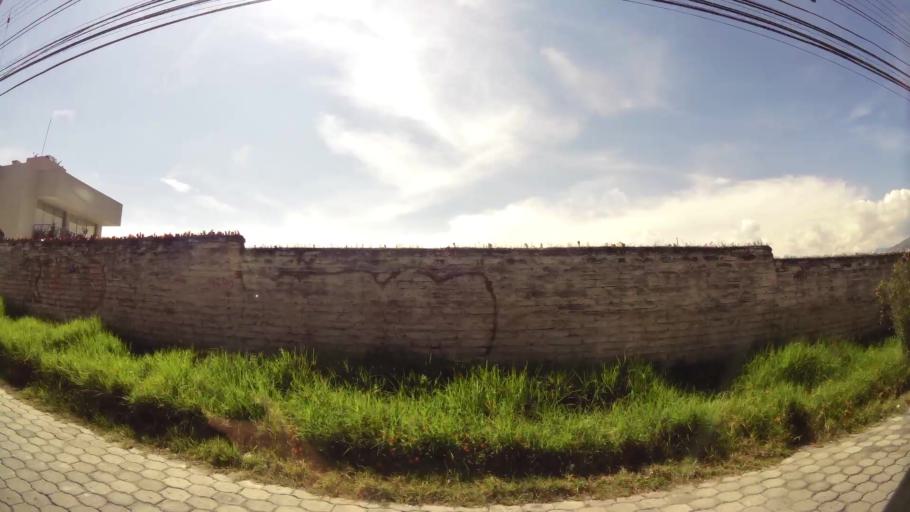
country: EC
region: Pichincha
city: Quito
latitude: -0.1983
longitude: -78.4460
